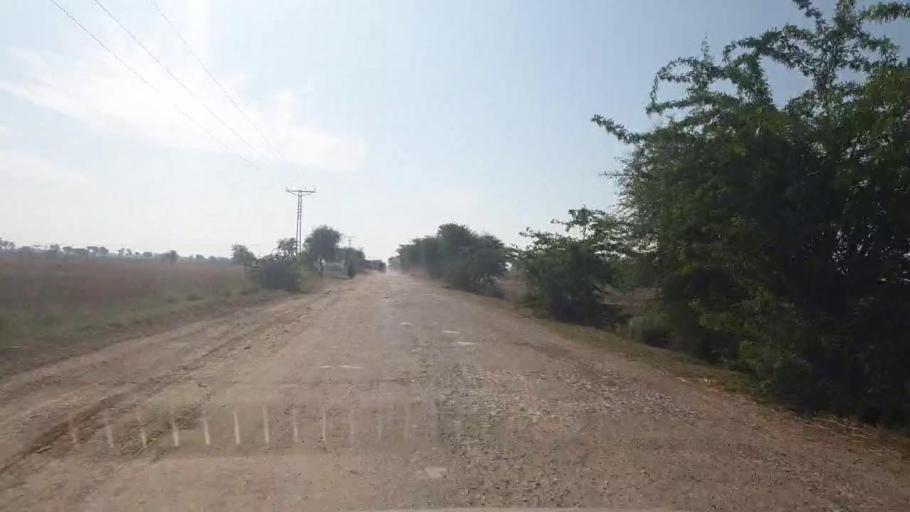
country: PK
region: Sindh
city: Talhar
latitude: 24.9077
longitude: 68.8206
